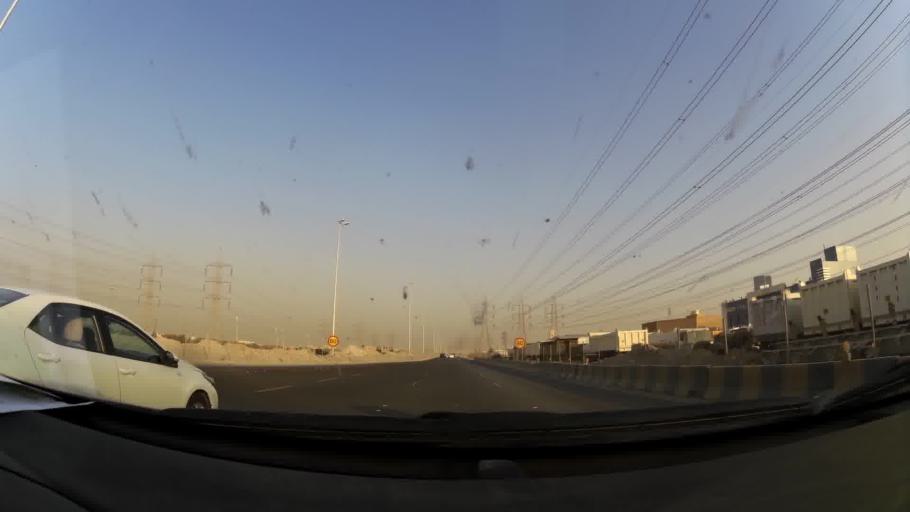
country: KW
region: Al Asimah
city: Ar Rabiyah
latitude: 29.2949
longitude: 47.8455
